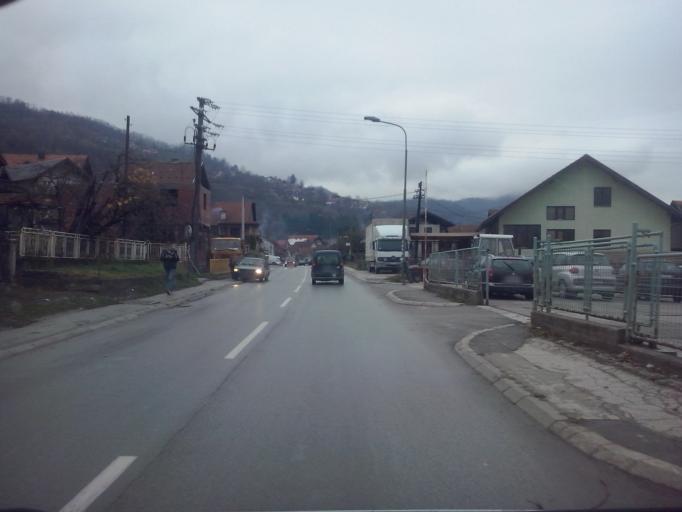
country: RS
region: Central Serbia
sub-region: Moravicki Okrug
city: Ivanjica
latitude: 43.5701
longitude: 20.2395
